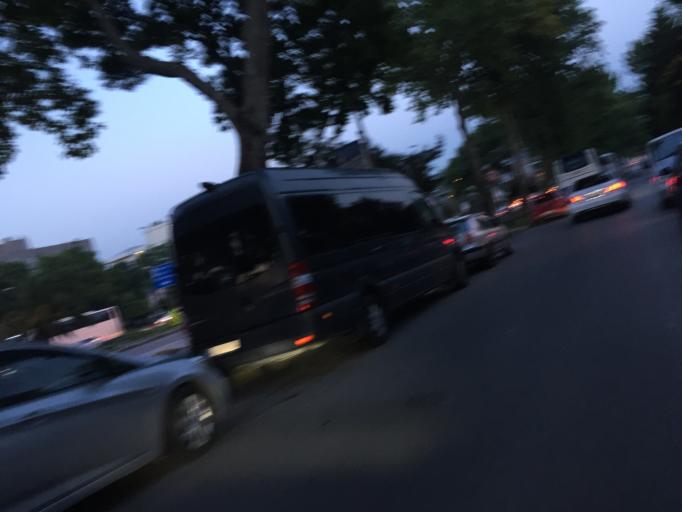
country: TR
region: Istanbul
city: Istanbul
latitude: 41.0228
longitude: 28.9310
